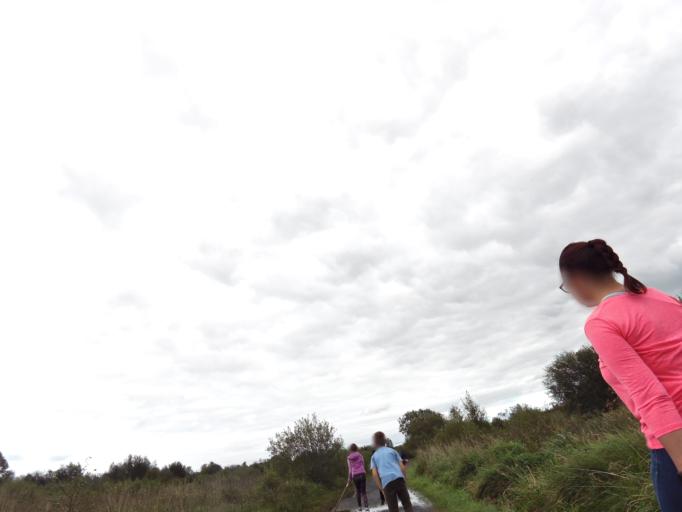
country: IE
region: Leinster
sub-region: Uibh Fhaili
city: Ferbane
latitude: 53.2224
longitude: -7.7370
